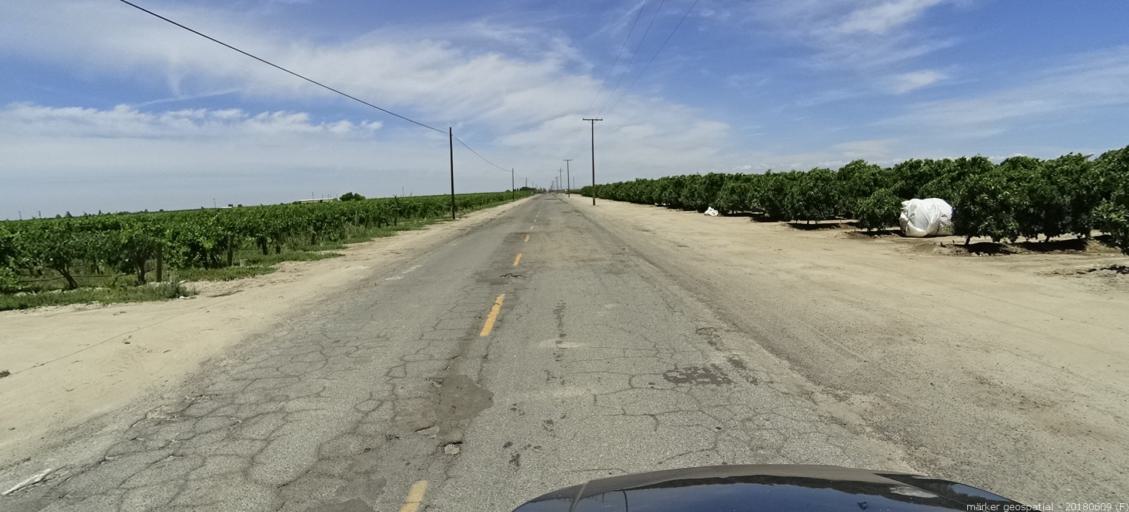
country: US
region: California
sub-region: Madera County
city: Parkwood
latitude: 36.8620
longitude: -120.0922
